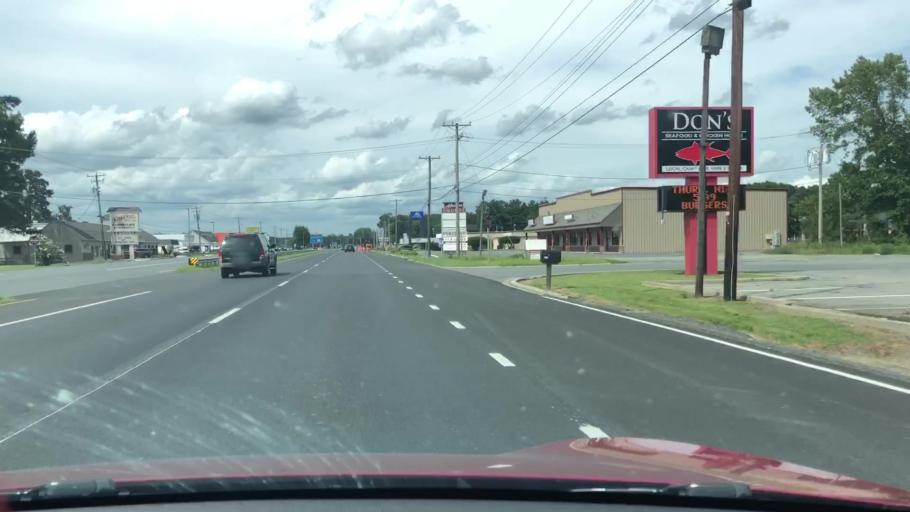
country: US
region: Maryland
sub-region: Worcester County
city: Pocomoke City
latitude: 38.0503
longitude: -75.5432
